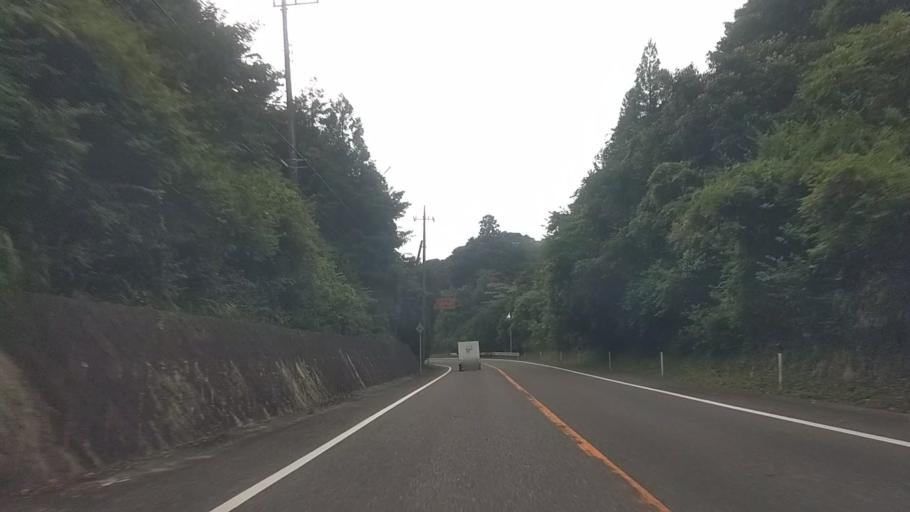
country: JP
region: Chiba
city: Kawaguchi
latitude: 35.1519
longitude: 140.0673
